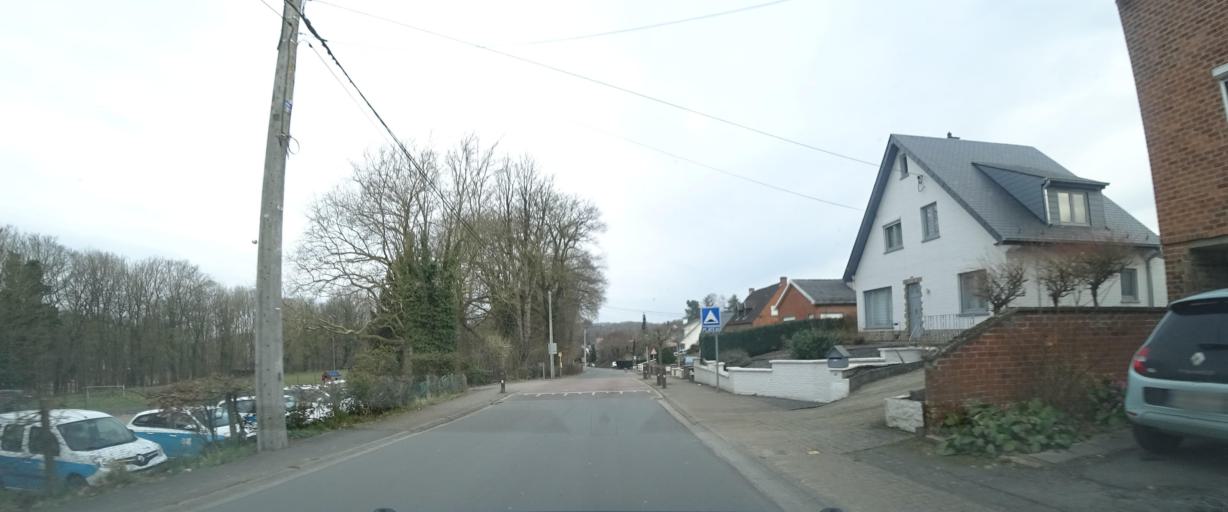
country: BE
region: Wallonia
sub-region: Province du Brabant Wallon
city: Mont-Saint-Guibert
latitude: 50.6290
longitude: 4.6172
